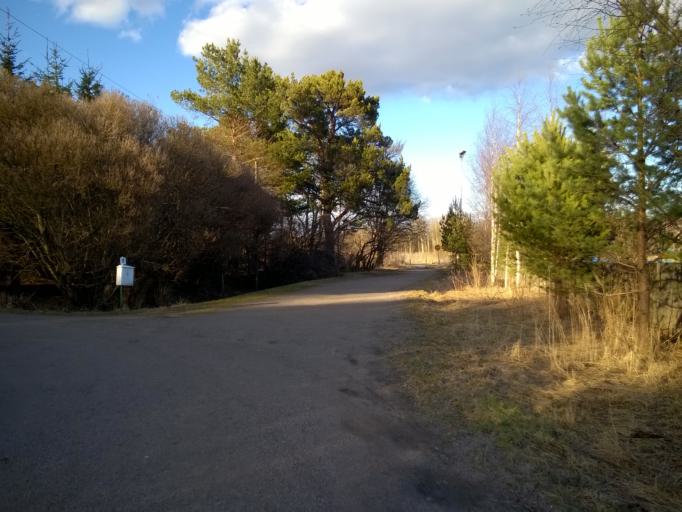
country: FI
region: Uusimaa
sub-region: Helsinki
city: Vantaa
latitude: 60.2449
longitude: 25.0401
